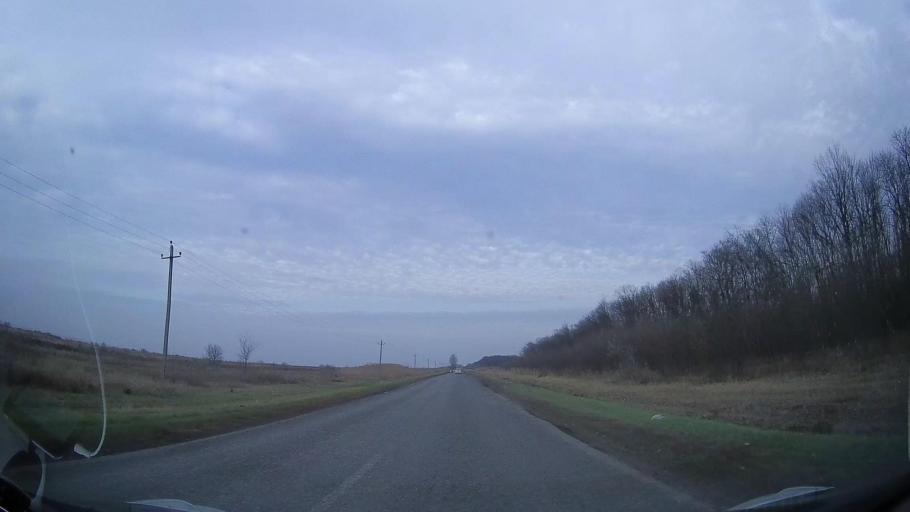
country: RU
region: Rostov
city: Ol'ginskaya
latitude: 47.1402
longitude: 39.8990
